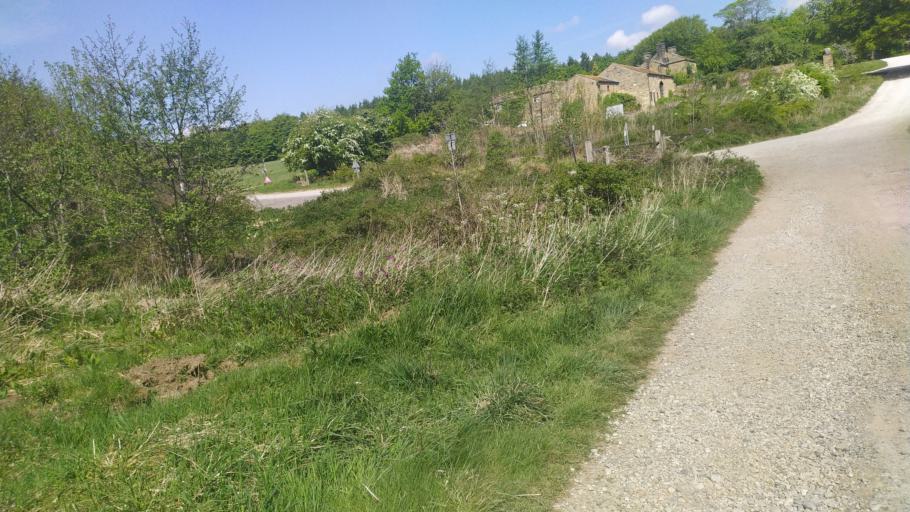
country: GB
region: England
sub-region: City and Borough of Leeds
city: Chapel Allerton
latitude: 53.8862
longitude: -1.5413
